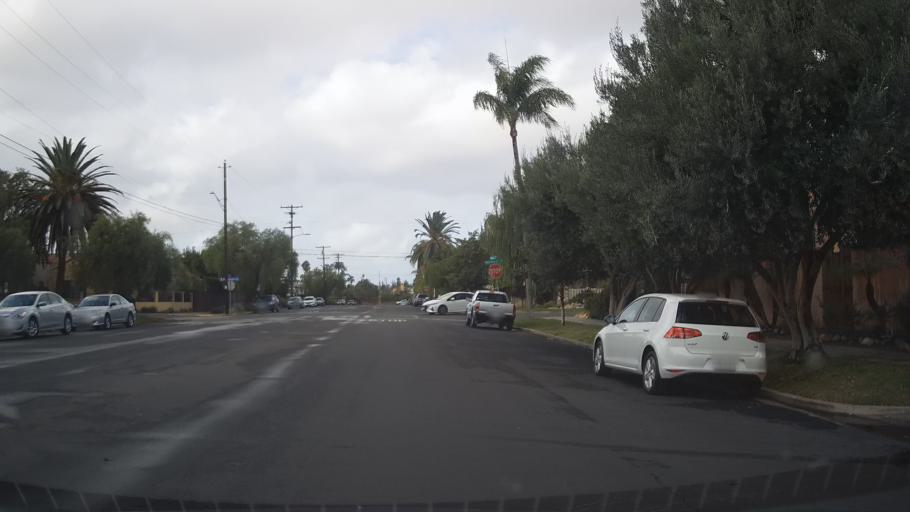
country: US
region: California
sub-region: San Diego County
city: San Diego
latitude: 32.7611
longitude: -117.1059
